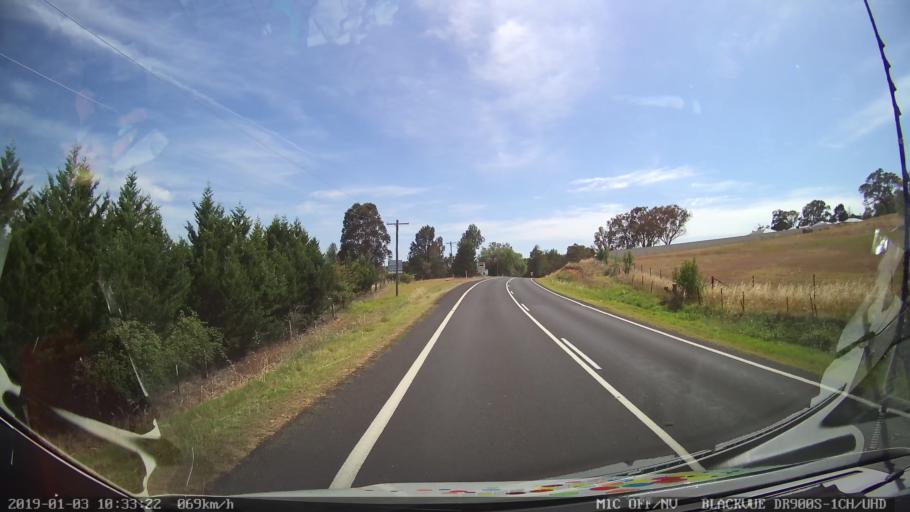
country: AU
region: New South Wales
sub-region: Young
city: Young
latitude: -34.3290
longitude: 148.2870
